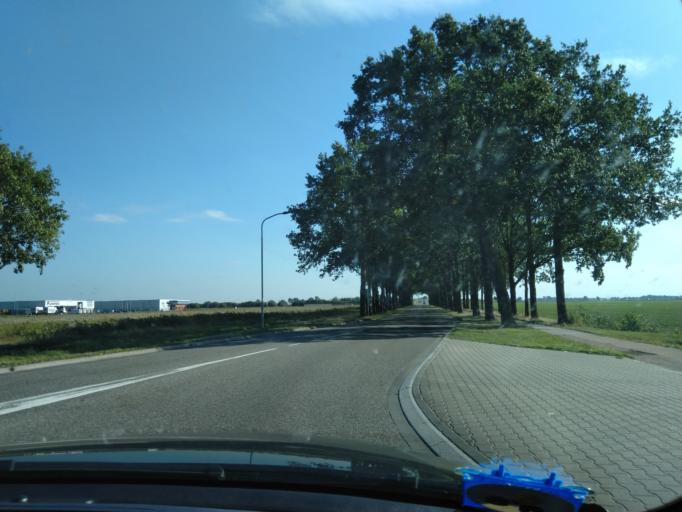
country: NL
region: Groningen
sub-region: Gemeente Veendam
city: Veendam
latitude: 53.0829
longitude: 6.8751
